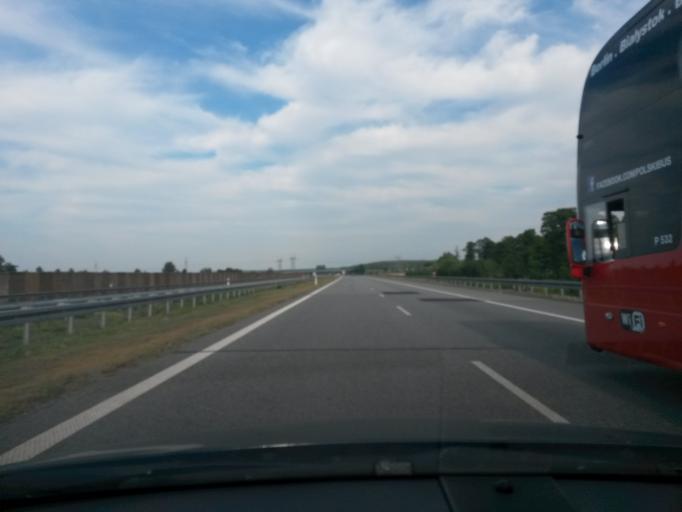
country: PL
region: Greater Poland Voivodeship
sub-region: Powiat koninski
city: Krzymow
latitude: 52.1425
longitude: 18.3937
